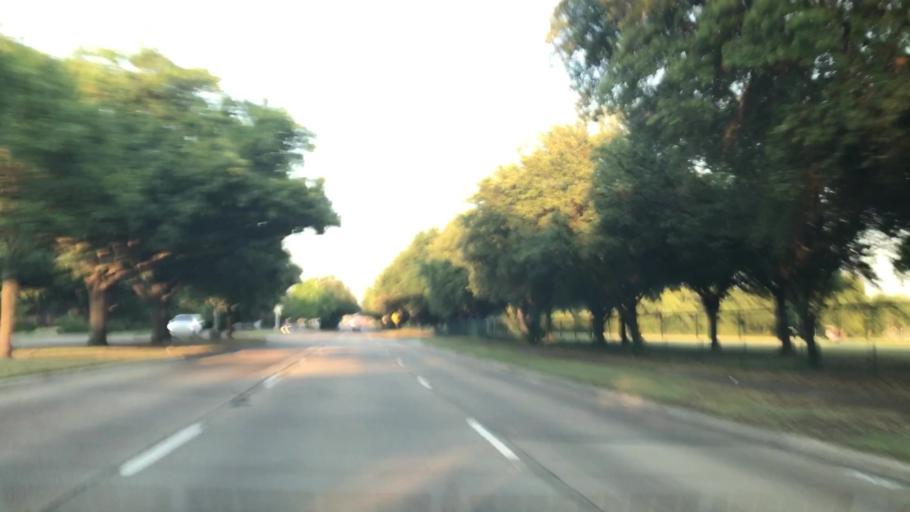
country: US
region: Texas
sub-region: Dallas County
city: Addison
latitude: 32.9094
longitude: -96.8231
